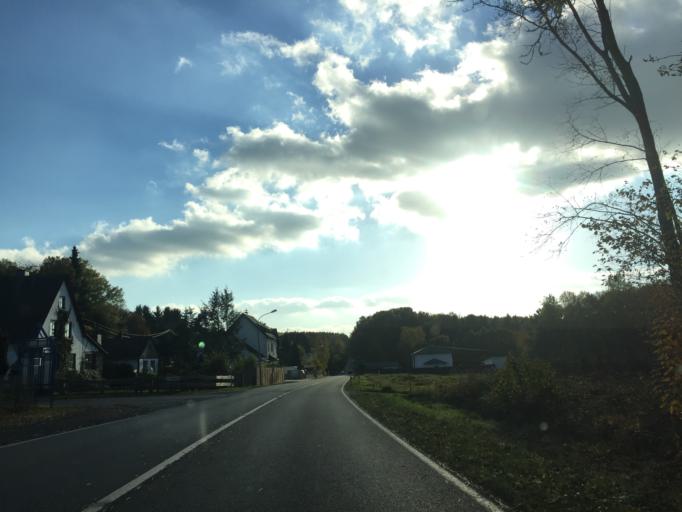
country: DE
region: Rheinland-Pfalz
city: Dreikirchen
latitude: 50.4493
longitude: 7.9438
